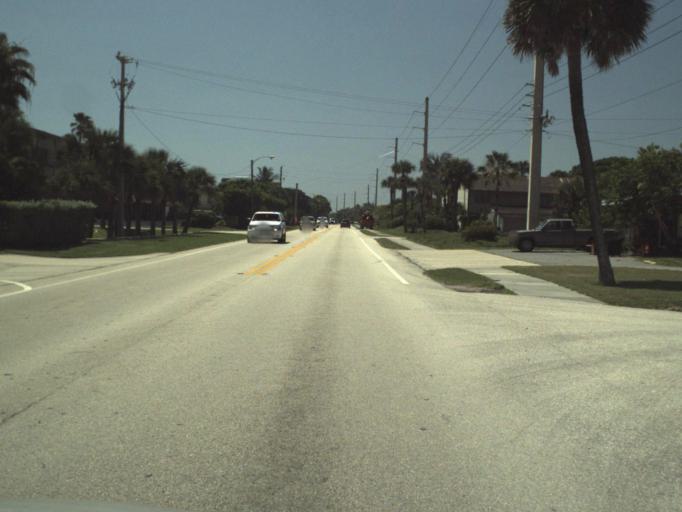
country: US
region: Florida
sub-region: Brevard County
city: Indialantic
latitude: 28.0882
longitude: -80.5656
